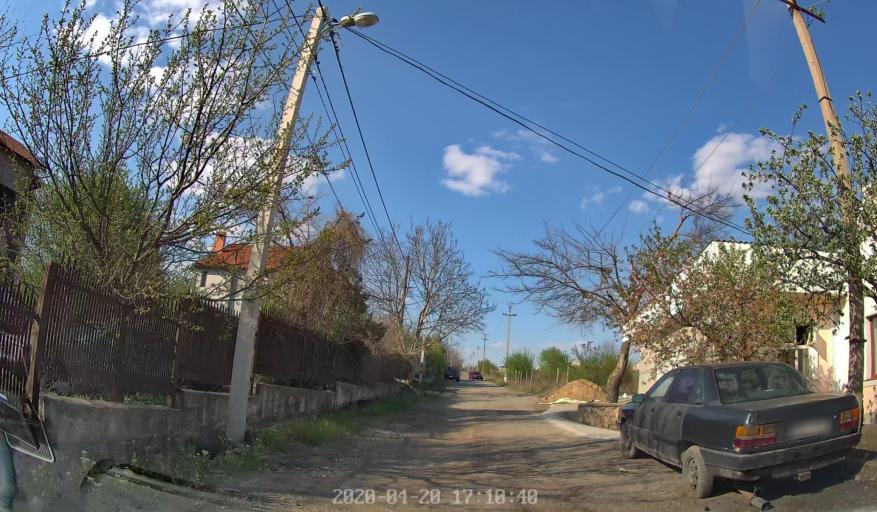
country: MD
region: Chisinau
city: Chisinau
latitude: 46.9623
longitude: 28.8408
